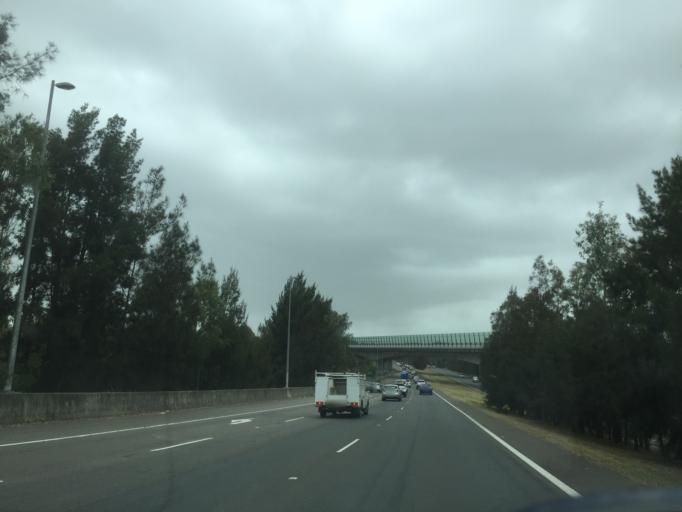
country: AU
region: New South Wales
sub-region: Blacktown
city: Blacktown
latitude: -33.7511
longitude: 150.9516
